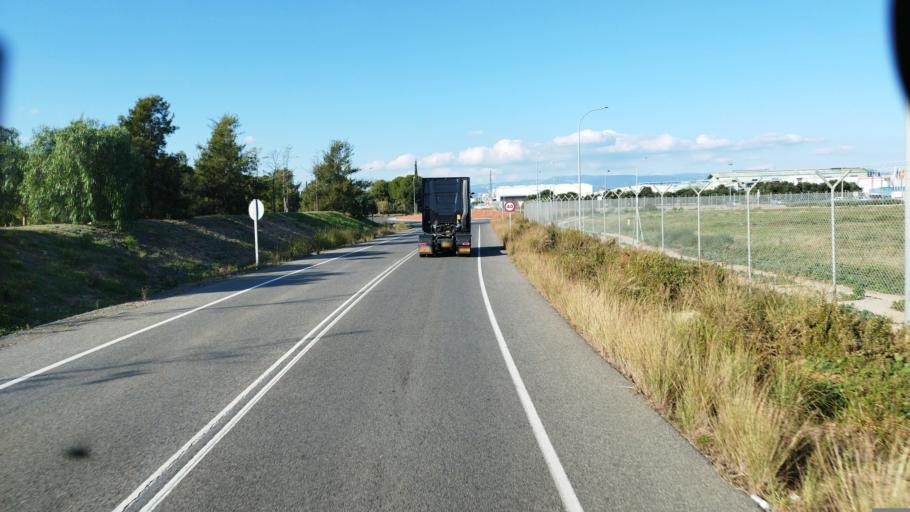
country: ES
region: Catalonia
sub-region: Provincia de Barcelona
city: La Pineda
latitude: 41.0950
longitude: 1.1734
